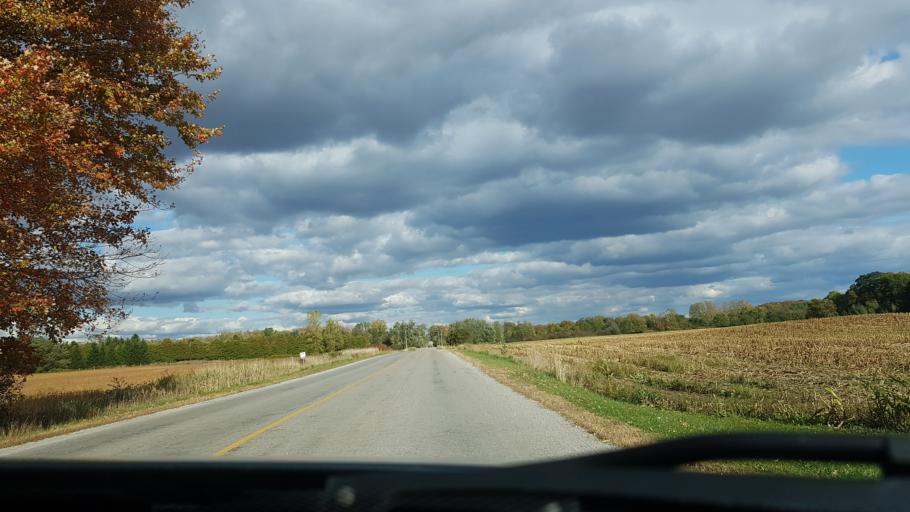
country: CA
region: Ontario
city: Delaware
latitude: 43.0078
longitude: -81.3925
